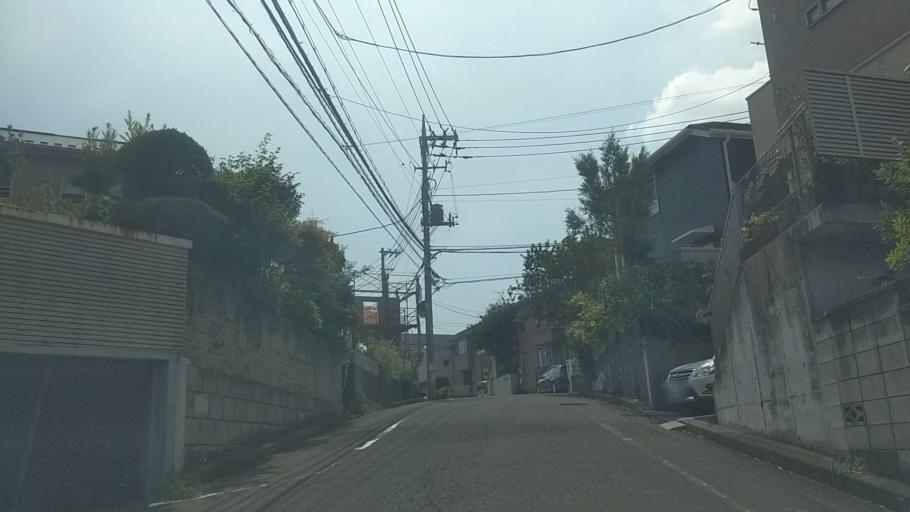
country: JP
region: Kanagawa
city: Yokohama
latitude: 35.5140
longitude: 139.6467
